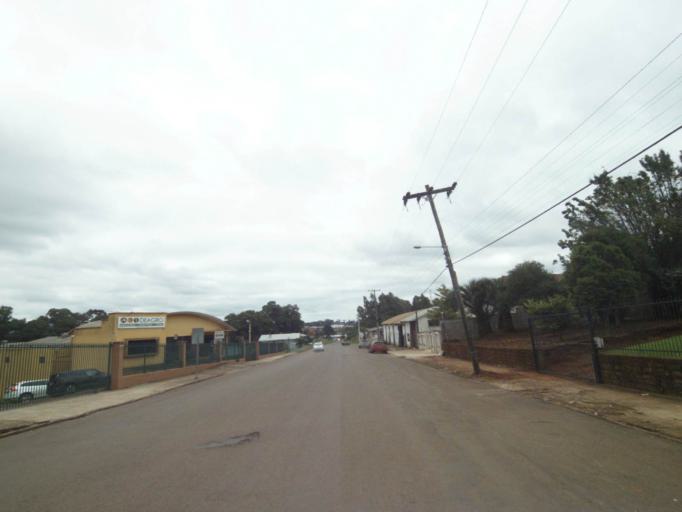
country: BR
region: Rio Grande do Sul
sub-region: Lagoa Vermelha
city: Lagoa Vermelha
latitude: -28.2117
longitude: -51.5318
